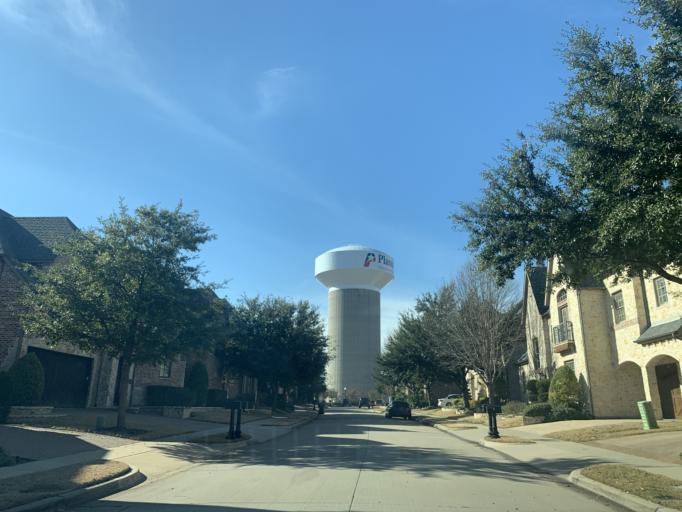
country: US
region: Texas
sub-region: Denton County
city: The Colony
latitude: 33.0577
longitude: -96.8195
